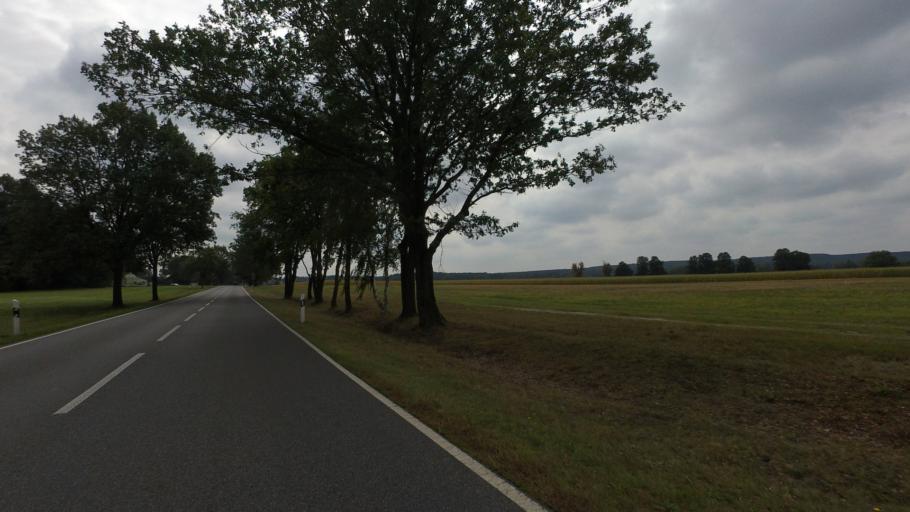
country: DE
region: Brandenburg
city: Luckau
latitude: 51.7827
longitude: 13.6881
